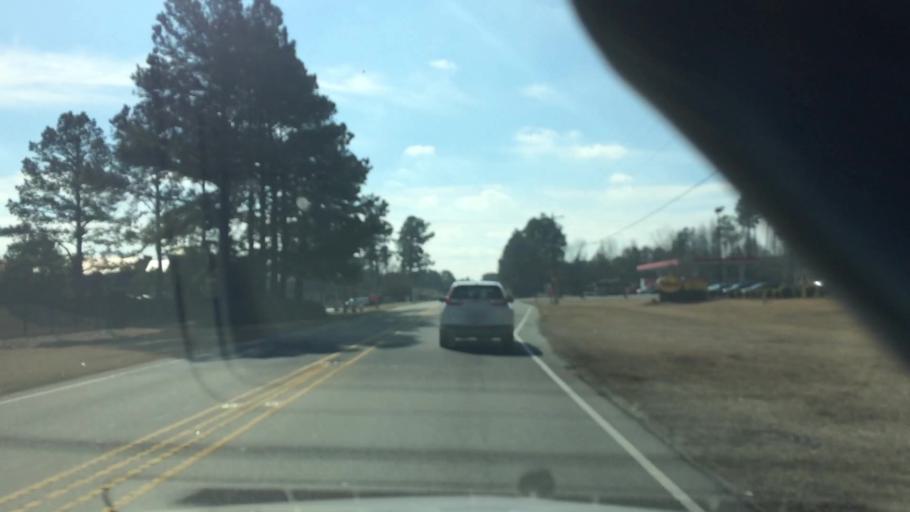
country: US
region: North Carolina
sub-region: Duplin County
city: Wallace
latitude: 34.7586
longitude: -77.9478
